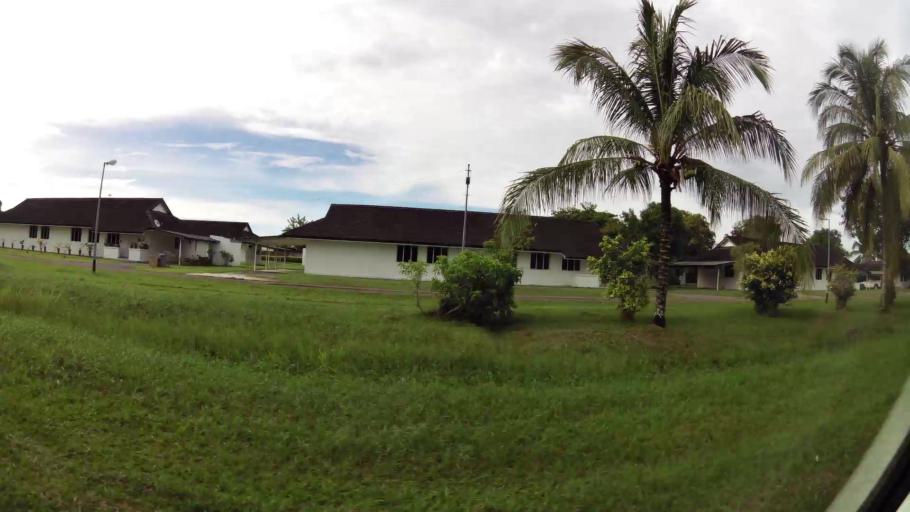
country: BN
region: Belait
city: Seria
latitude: 4.6100
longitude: 114.3249
